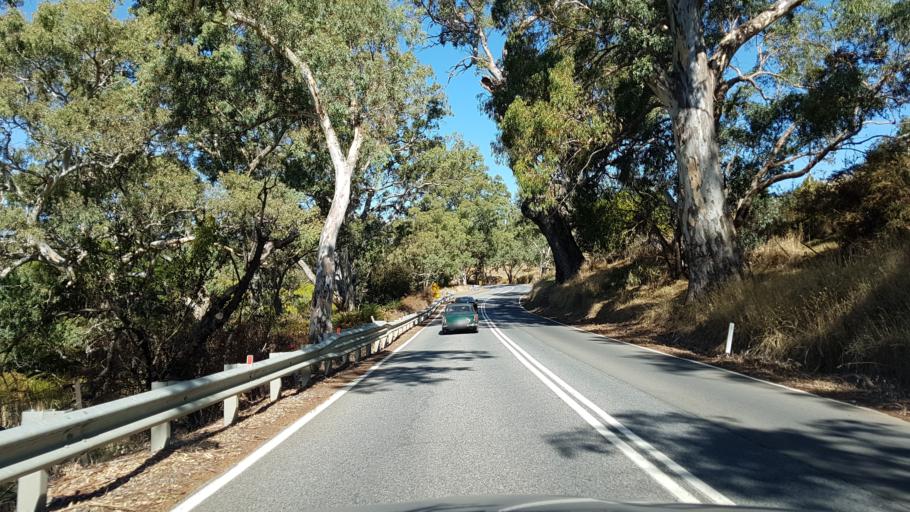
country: AU
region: South Australia
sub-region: Adelaide Hills
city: Birdwood
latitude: -34.8243
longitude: 138.9299
